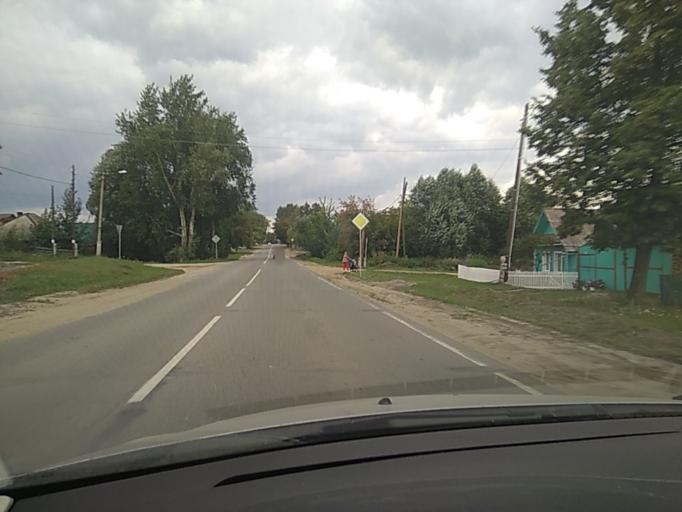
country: RU
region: Chelyabinsk
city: Kyshtym
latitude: 55.7059
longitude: 60.5187
